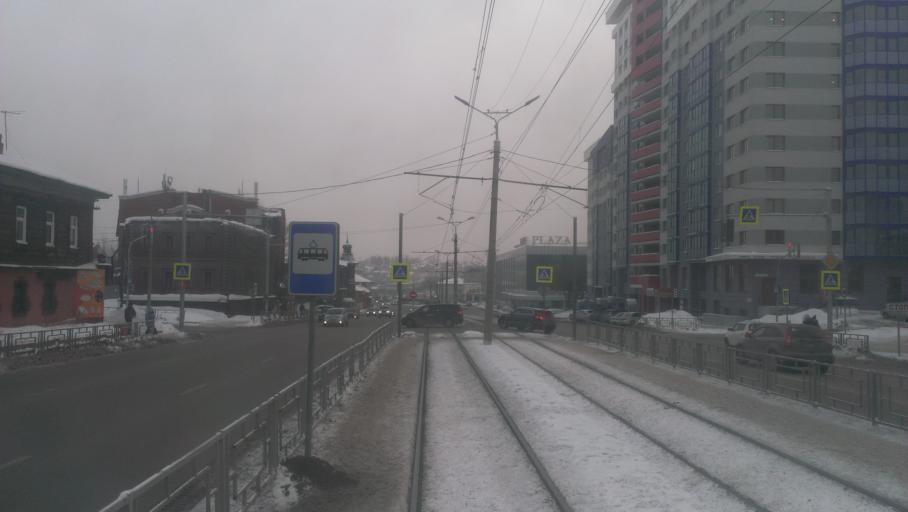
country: RU
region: Altai Krai
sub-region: Gorod Barnaulskiy
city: Barnaul
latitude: 53.3326
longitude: 83.7802
